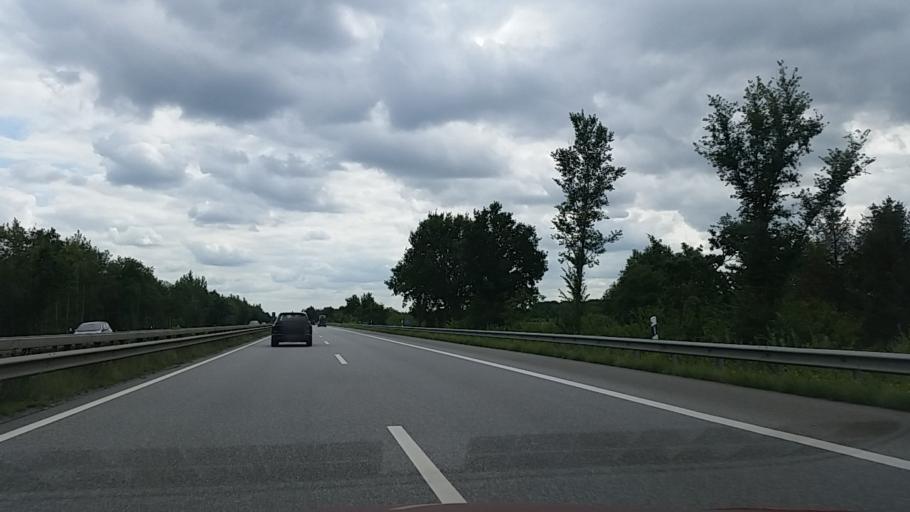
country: DE
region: Lower Saxony
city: Driftsethe
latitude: 53.4301
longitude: 8.5807
